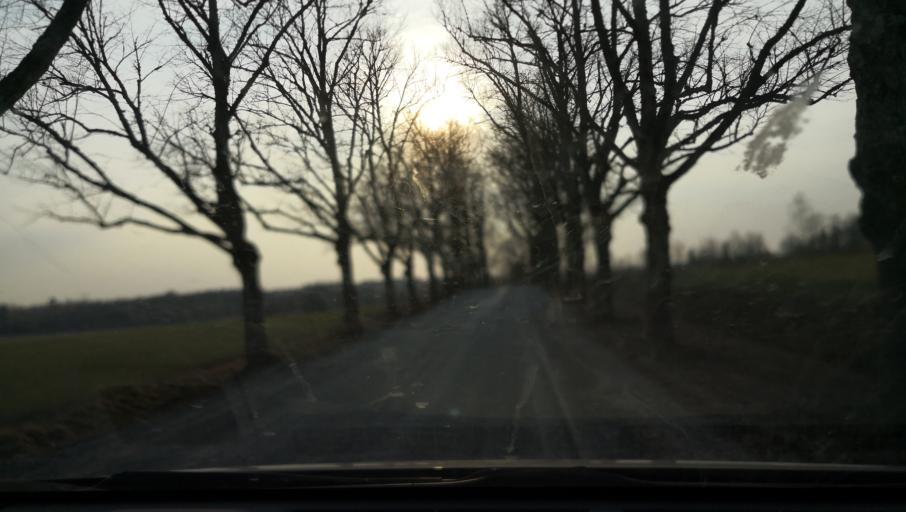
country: SE
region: OErebro
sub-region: Orebro Kommun
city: Hovsta
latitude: 59.3885
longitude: 15.2547
